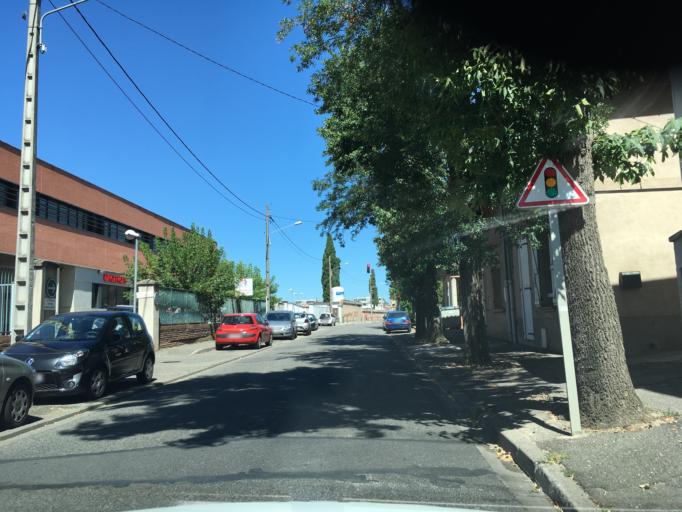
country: FR
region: Midi-Pyrenees
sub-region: Departement du Tarn-et-Garonne
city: Montauban
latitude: 44.0228
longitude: 1.3532
